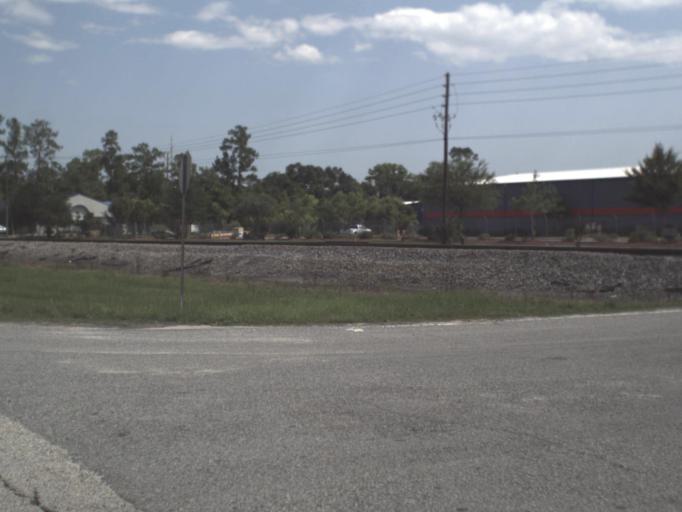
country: US
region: Florida
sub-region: Alachua County
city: Gainesville
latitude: 29.7001
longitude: -82.3398
